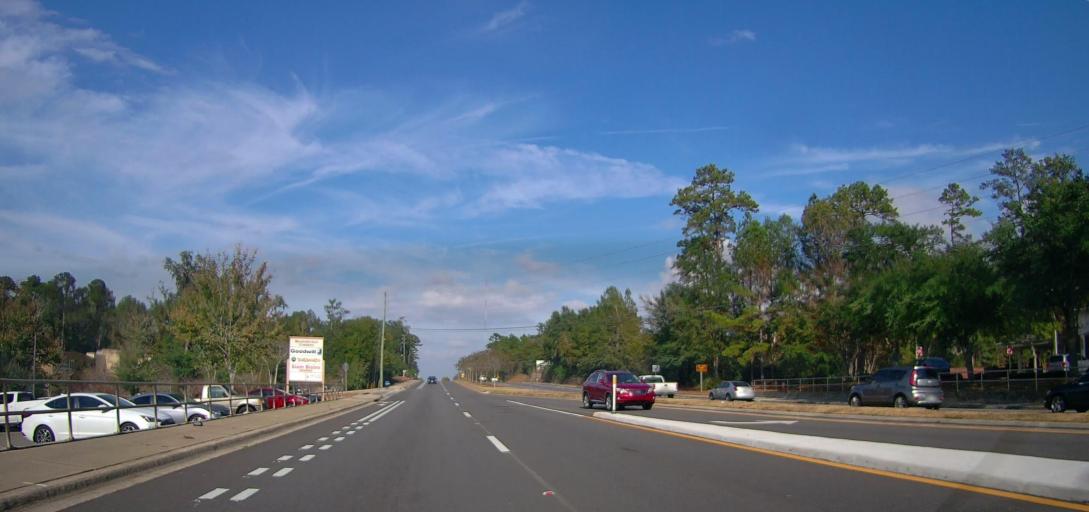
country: US
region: Florida
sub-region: Leon County
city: Tallahassee
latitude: 30.5646
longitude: -84.2144
